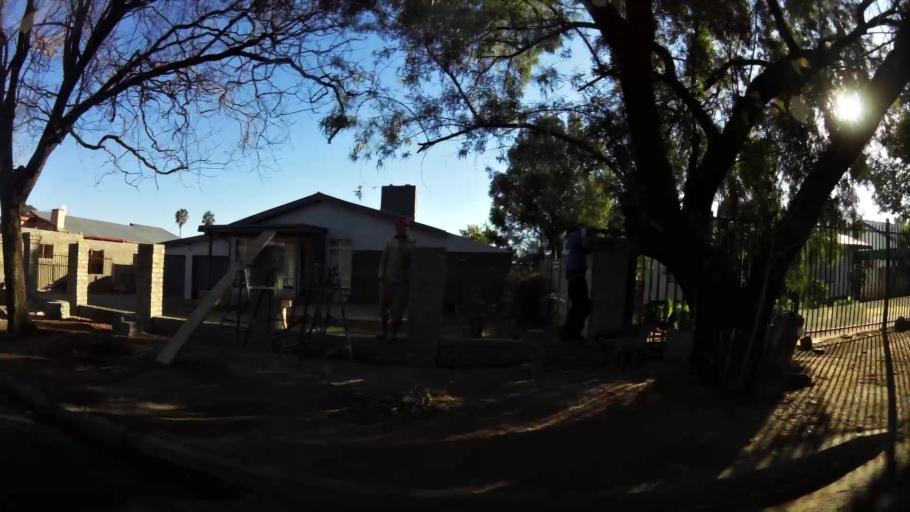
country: ZA
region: Northern Cape
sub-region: Frances Baard District Municipality
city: Kimberley
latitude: -28.7388
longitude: 24.7346
